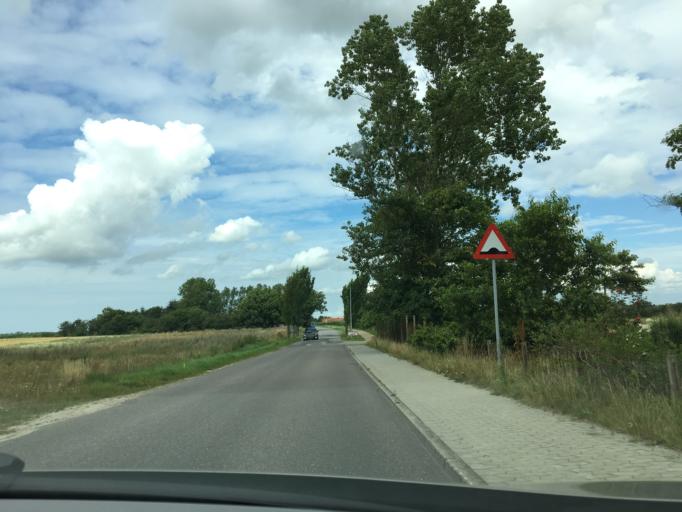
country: DK
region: South Denmark
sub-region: Varde Kommune
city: Oksbol
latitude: 55.6576
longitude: 8.2921
